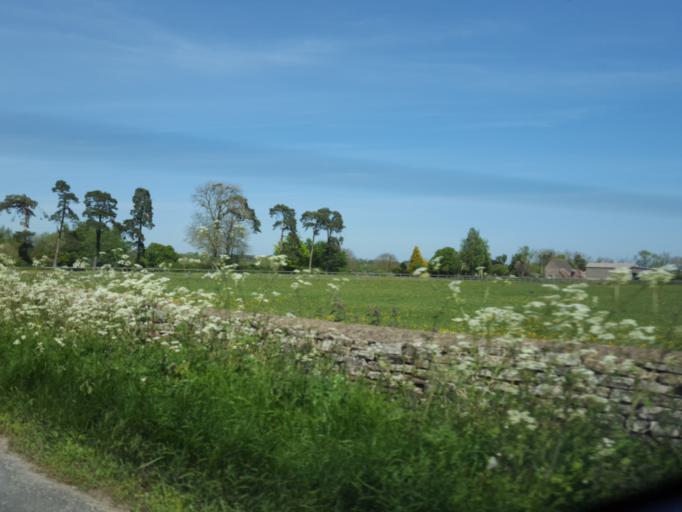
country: GB
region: England
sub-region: Wiltshire
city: Hankerton
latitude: 51.6254
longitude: -2.0753
